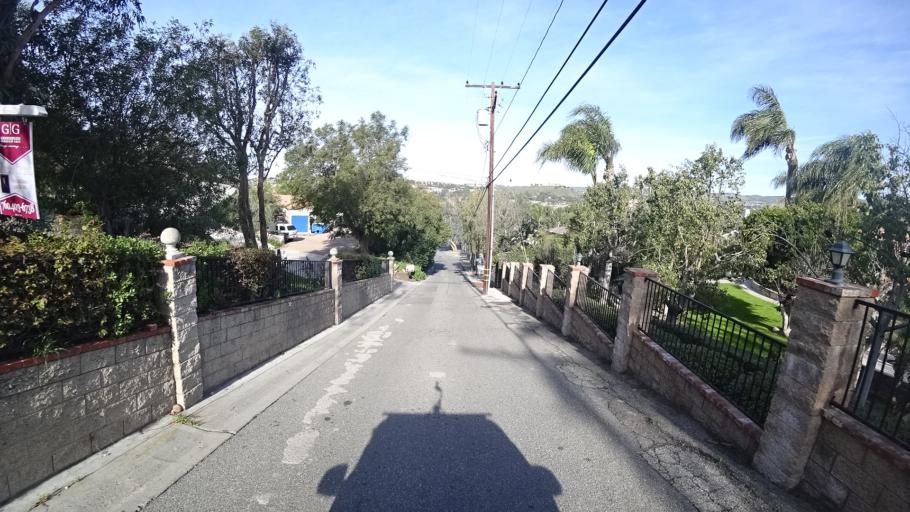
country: US
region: California
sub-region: Orange County
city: Yorba Linda
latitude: 33.8644
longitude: -117.7620
